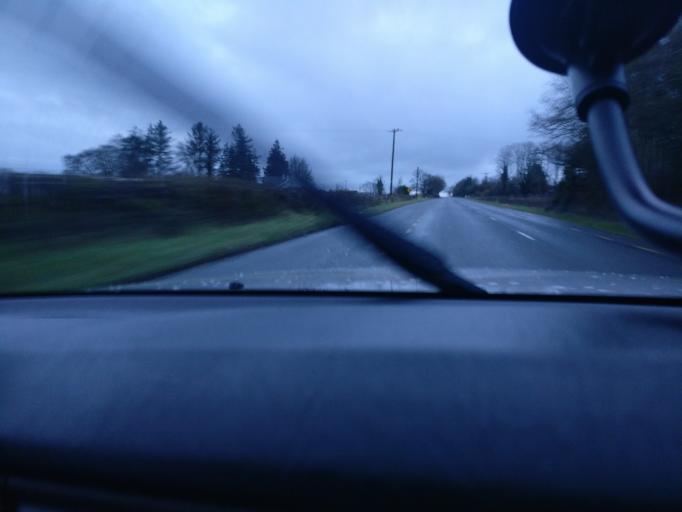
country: IE
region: Connaught
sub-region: County Galway
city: Loughrea
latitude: 53.2665
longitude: -8.4149
